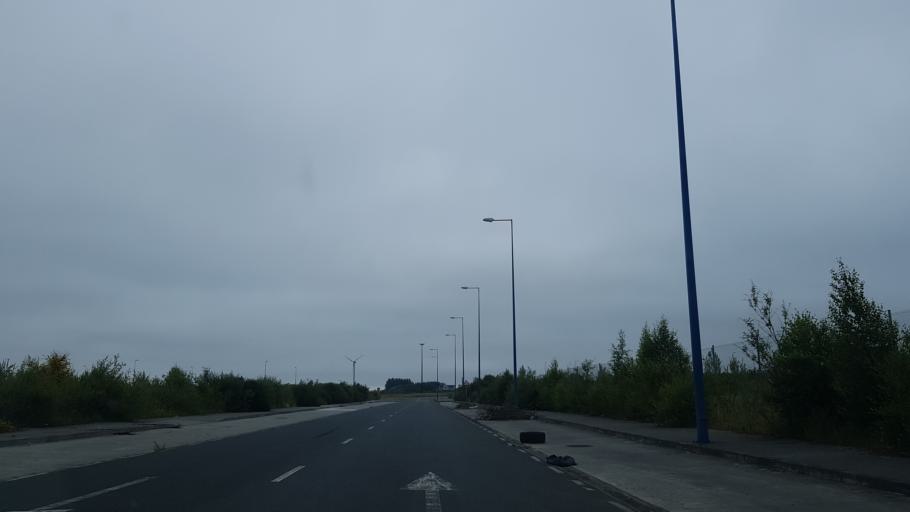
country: ES
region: Galicia
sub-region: Provincia de Lugo
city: Lugo
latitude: 43.0451
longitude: -7.5549
